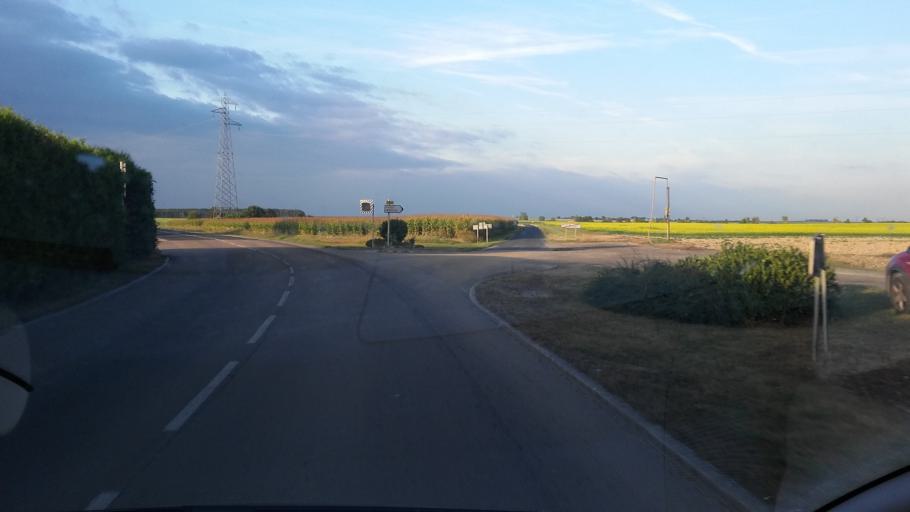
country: FR
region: Champagne-Ardenne
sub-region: Departement de la Marne
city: Fere-Champenoise
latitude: 48.8143
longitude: 3.9947
